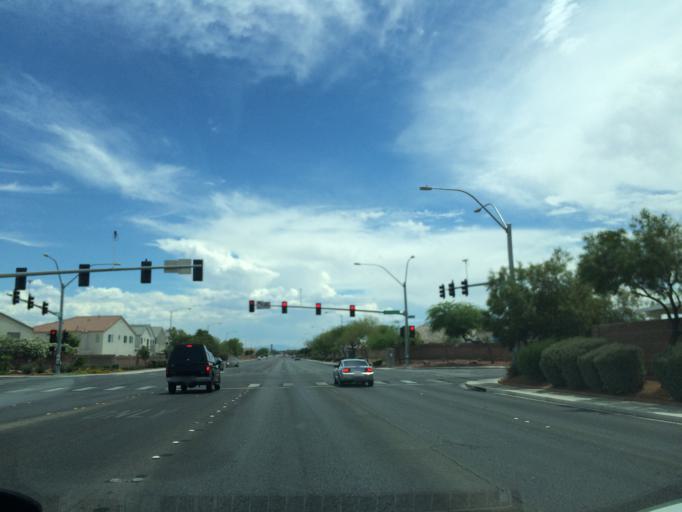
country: US
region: Nevada
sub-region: Clark County
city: North Las Vegas
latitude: 36.2547
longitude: -115.1801
